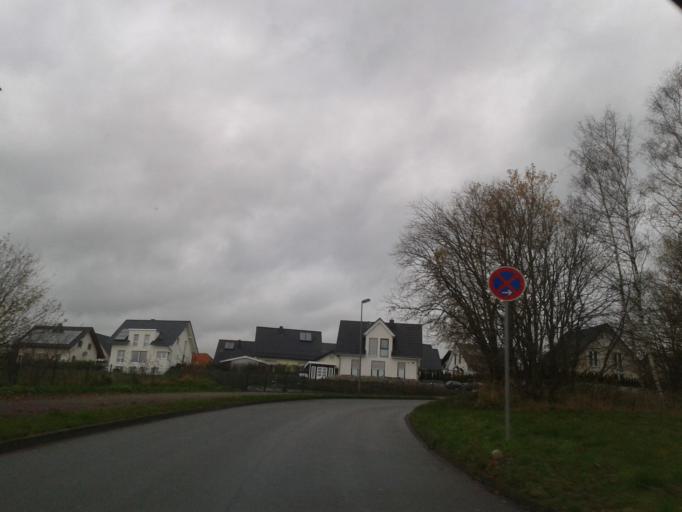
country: DE
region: North Rhine-Westphalia
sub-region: Regierungsbezirk Detmold
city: Blomberg
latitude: 51.9377
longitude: 9.1035
